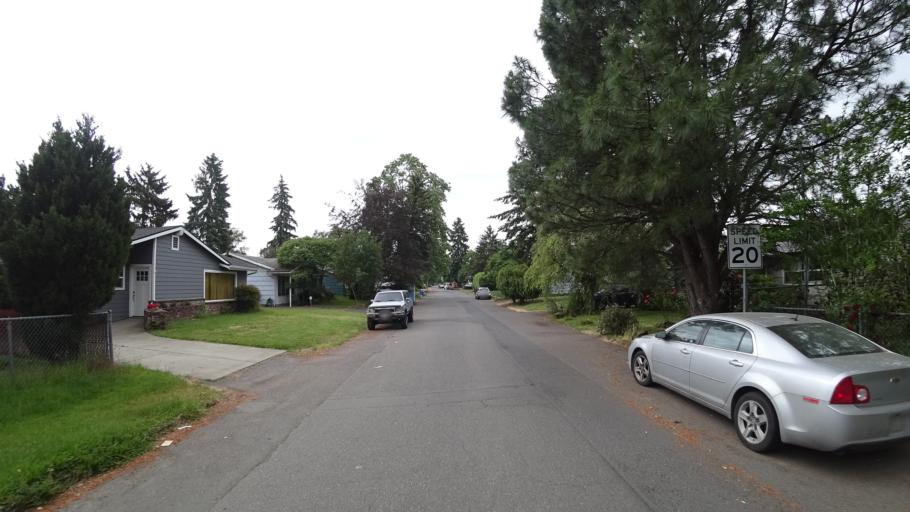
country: US
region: Oregon
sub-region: Multnomah County
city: Lents
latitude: 45.4757
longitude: -122.5841
